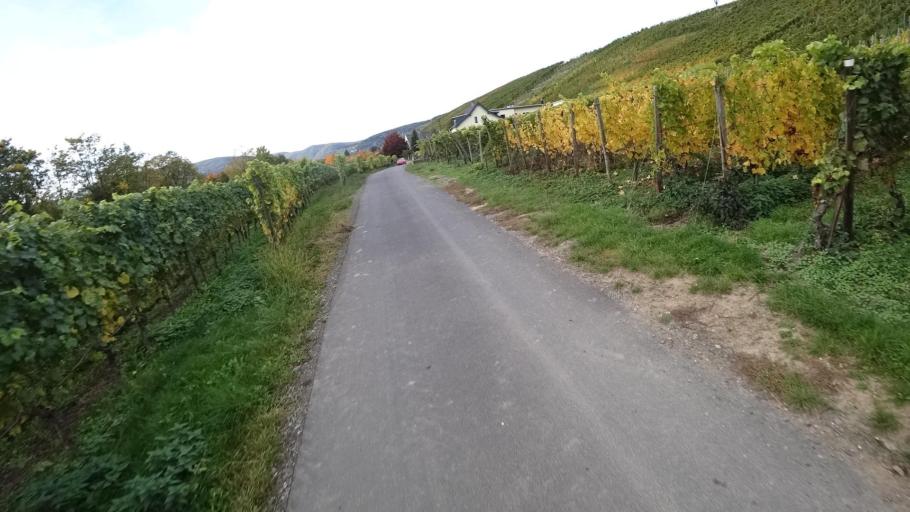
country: DE
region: Rheinland-Pfalz
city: Bad Neuenahr-Ahrweiler
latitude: 50.5479
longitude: 7.1101
